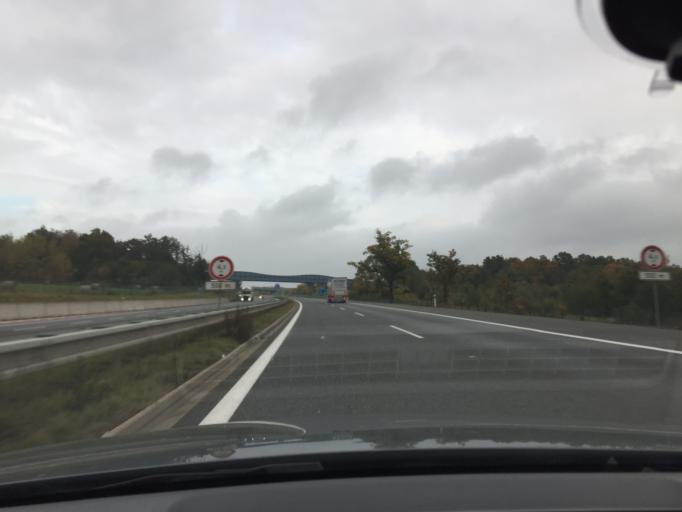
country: CZ
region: Ustecky
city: Chlumec
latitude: 50.7186
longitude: 13.9930
